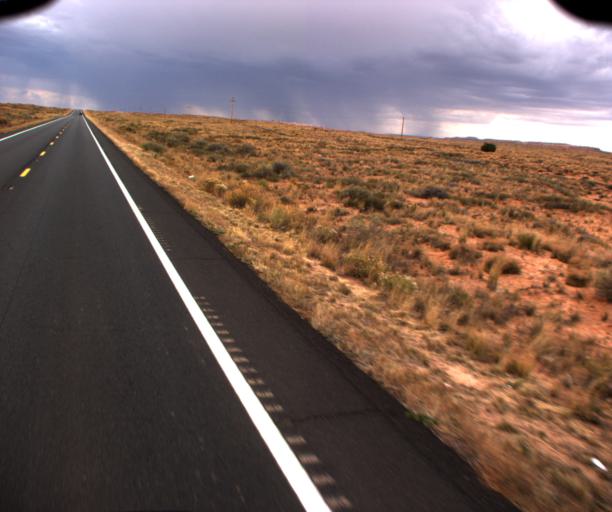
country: US
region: Arizona
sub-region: Coconino County
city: Kaibito
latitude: 36.3014
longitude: -110.9755
